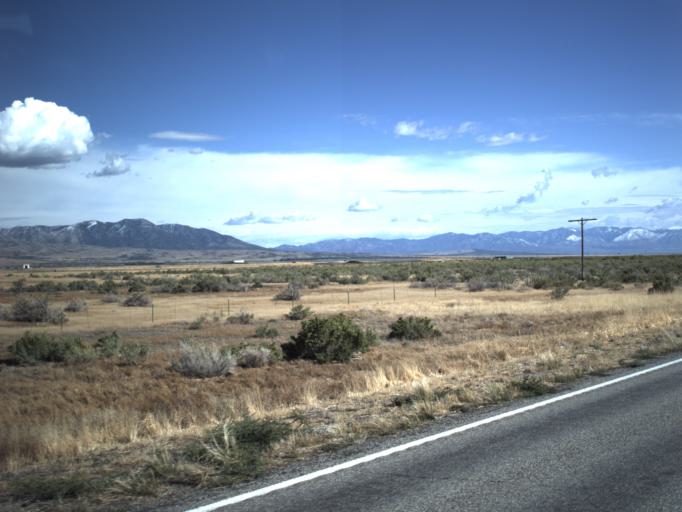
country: US
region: Utah
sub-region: Millard County
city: Delta
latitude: 39.3310
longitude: -112.4873
